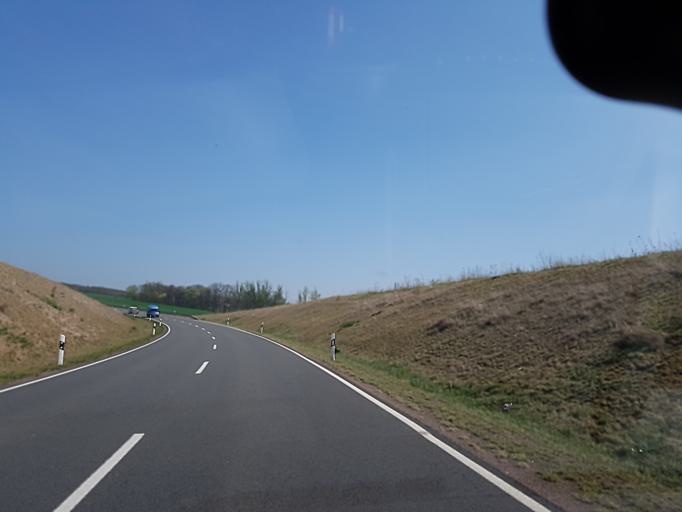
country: DE
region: Saxony
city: Wermsdorf
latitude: 51.2722
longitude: 12.9413
